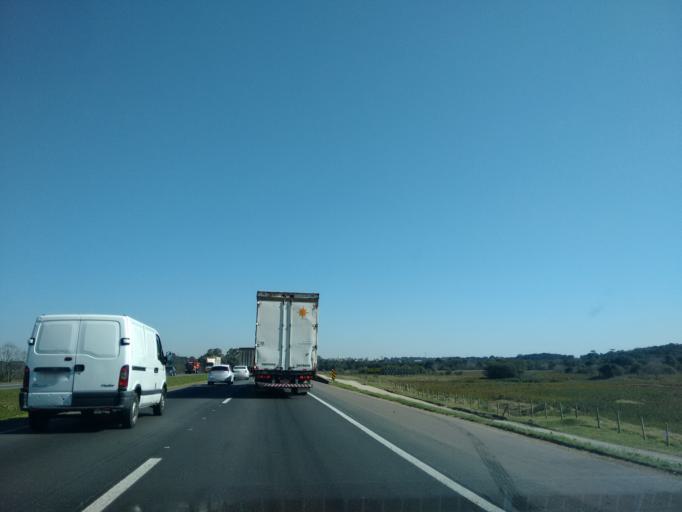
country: BR
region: Parana
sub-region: Sao Jose Dos Pinhais
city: Sao Jose dos Pinhais
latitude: -25.5681
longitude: -49.2329
